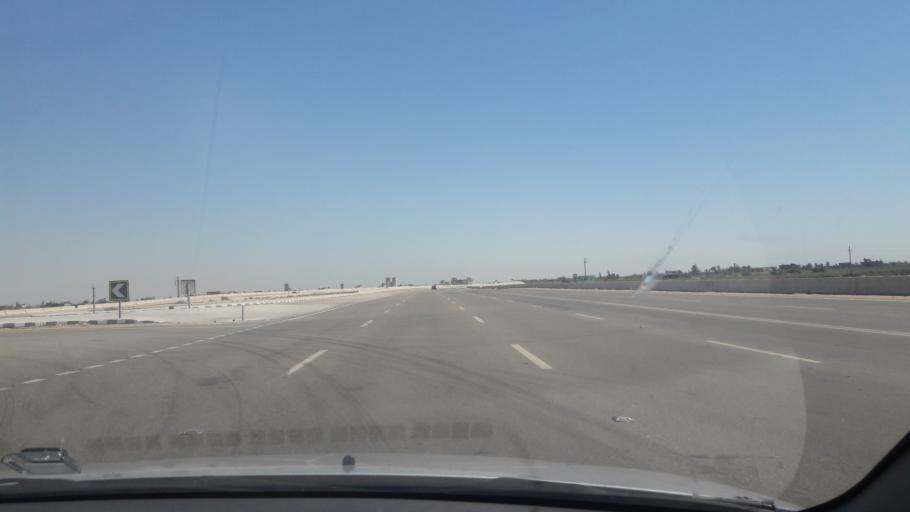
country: EG
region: Muhafazat Bur Sa`id
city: Port Said
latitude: 31.0694
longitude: 32.2349
